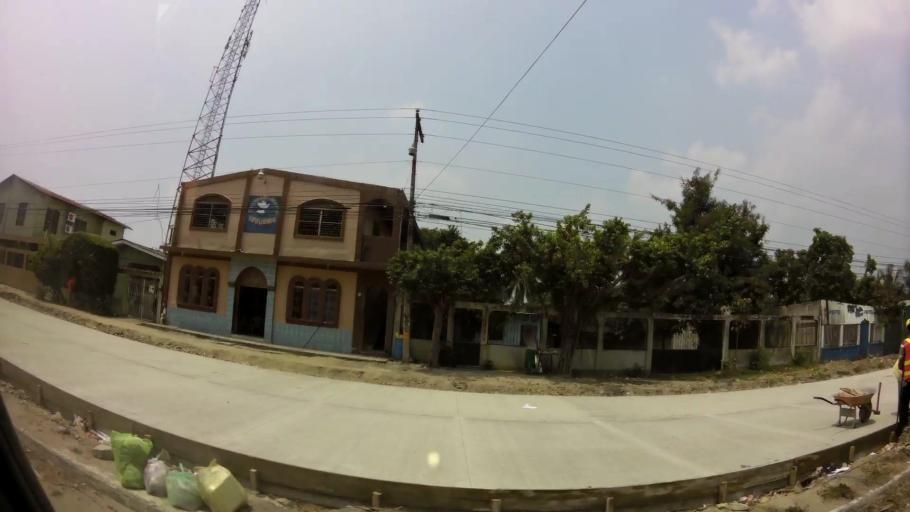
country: HN
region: Cortes
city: San Pedro Sula
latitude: 15.4792
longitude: -88.0089
